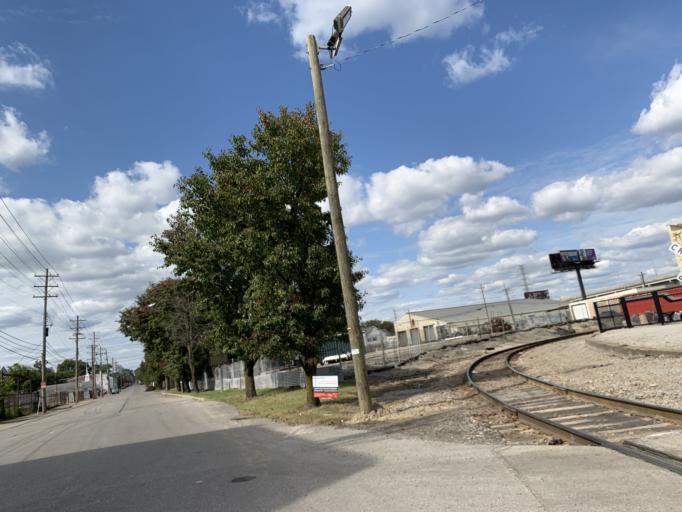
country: US
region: Kentucky
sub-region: Jefferson County
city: Louisville
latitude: 38.2622
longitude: -85.7741
